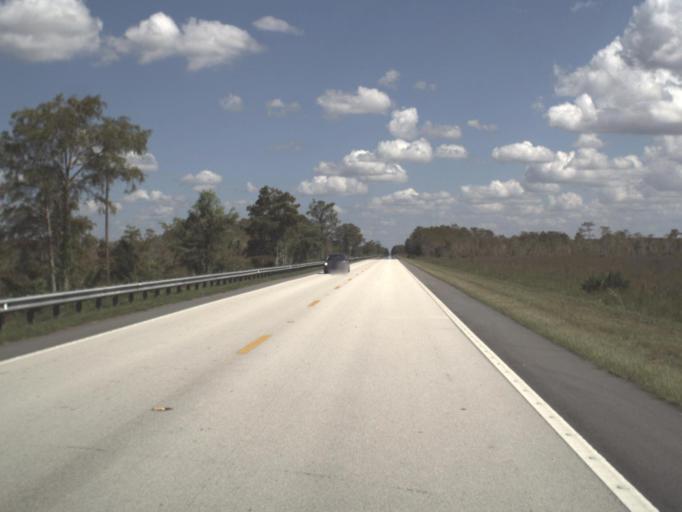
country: US
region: Florida
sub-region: Collier County
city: Immokalee
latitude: 25.8622
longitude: -81.0863
